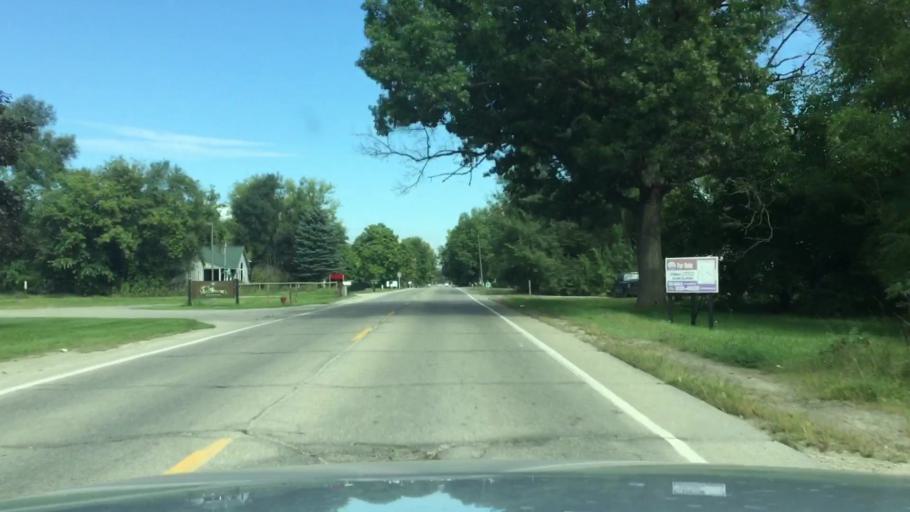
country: US
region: Michigan
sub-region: Wayne County
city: Belleville
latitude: 42.1623
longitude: -83.4824
